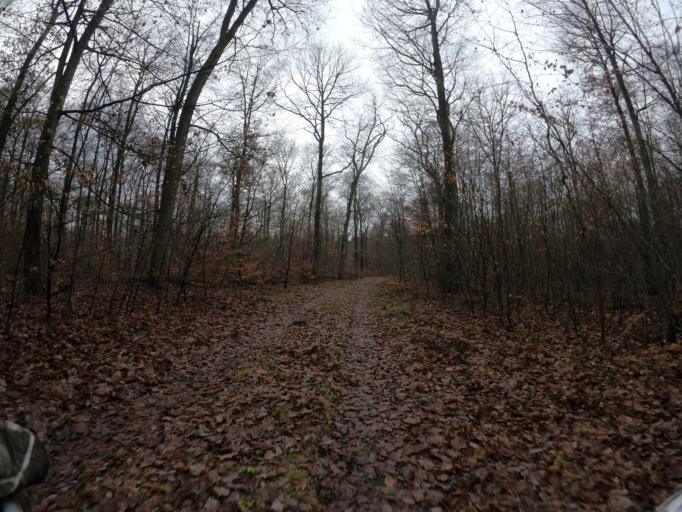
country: DE
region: Hesse
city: Morfelden-Walldorf
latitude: 50.0199
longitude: 8.6034
